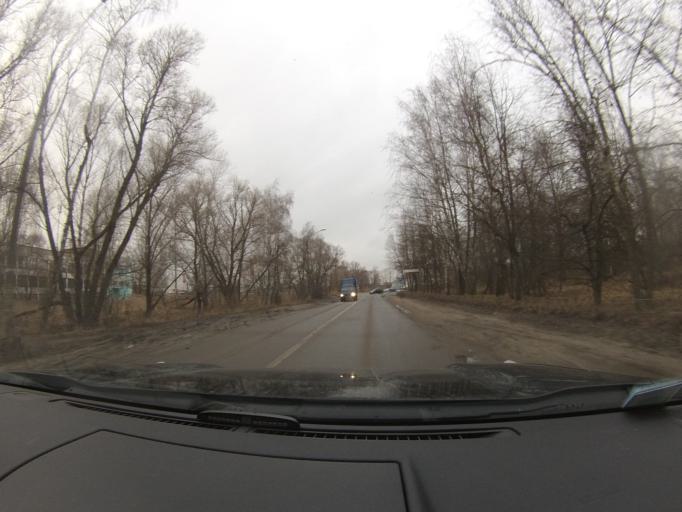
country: RU
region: Moskovskaya
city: Lopatinskiy
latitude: 55.3403
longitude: 38.7300
